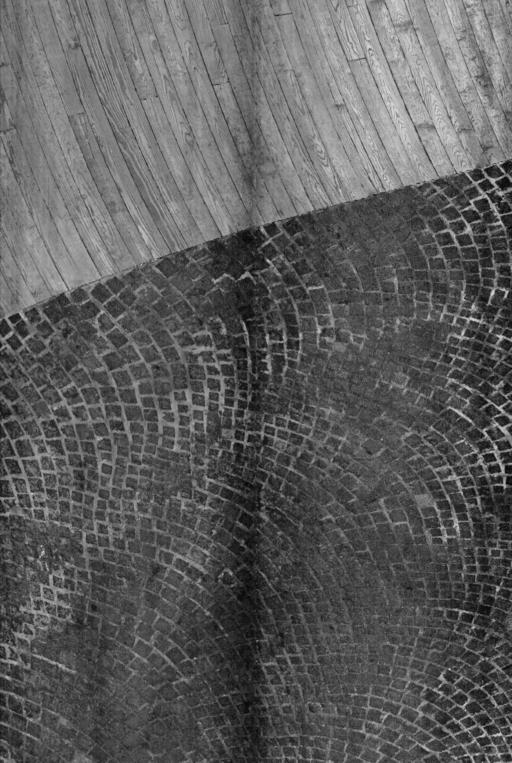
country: US
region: Washington, D.C.
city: Washington, D.C.
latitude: 38.8800
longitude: -77.0254
